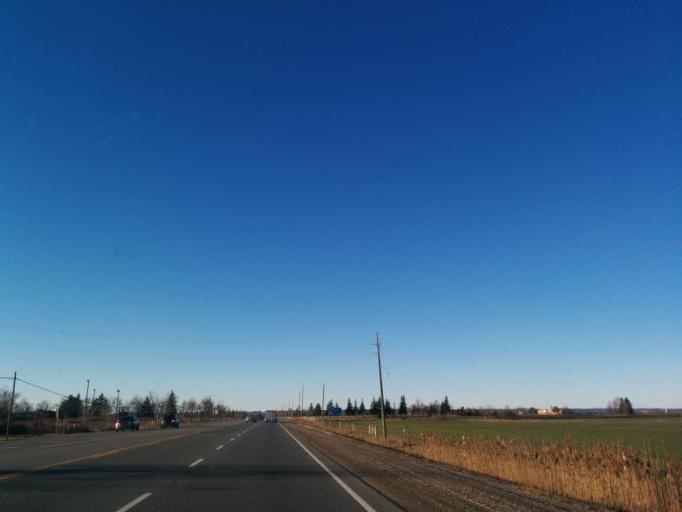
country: CA
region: Ontario
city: Brampton
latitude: 43.7757
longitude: -79.8812
